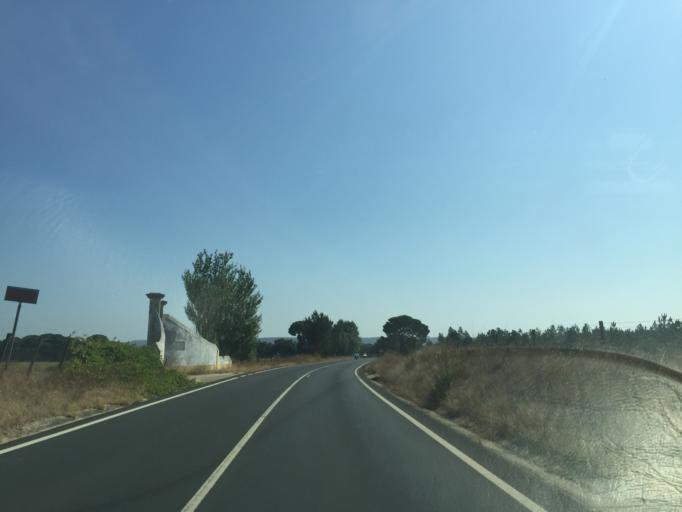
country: PT
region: Santarem
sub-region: Alpiarca
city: Alpiarca
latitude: 39.2755
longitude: -8.5511
